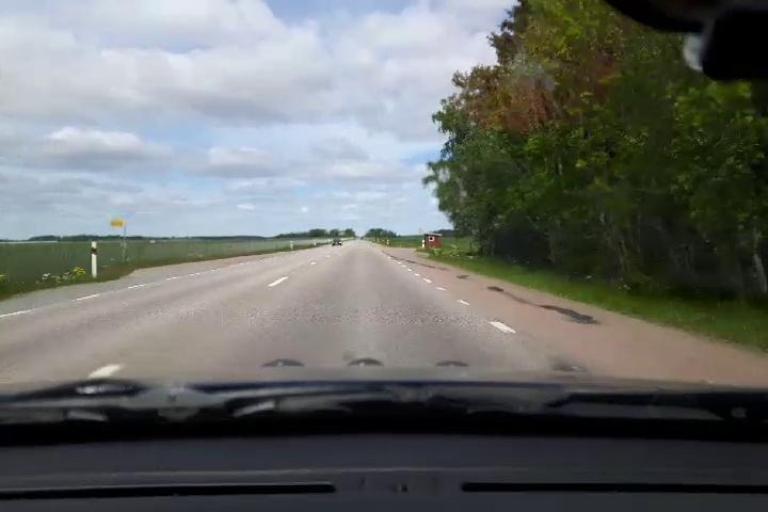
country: SE
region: Uppsala
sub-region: Uppsala Kommun
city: Gamla Uppsala
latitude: 59.8932
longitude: 17.6160
